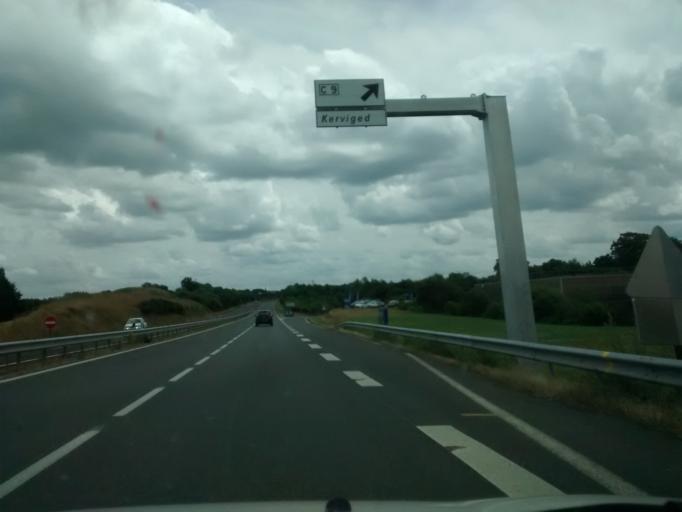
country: FR
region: Brittany
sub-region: Departement des Cotes-d'Armor
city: Cavan
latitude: 48.6849
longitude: -3.3625
